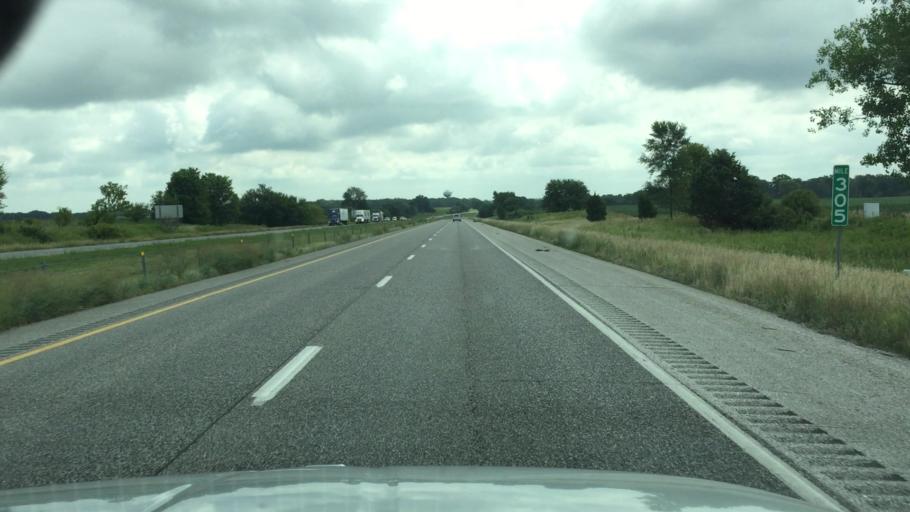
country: US
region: Illinois
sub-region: Rock Island County
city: Hampton
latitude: 41.5953
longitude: -90.3884
